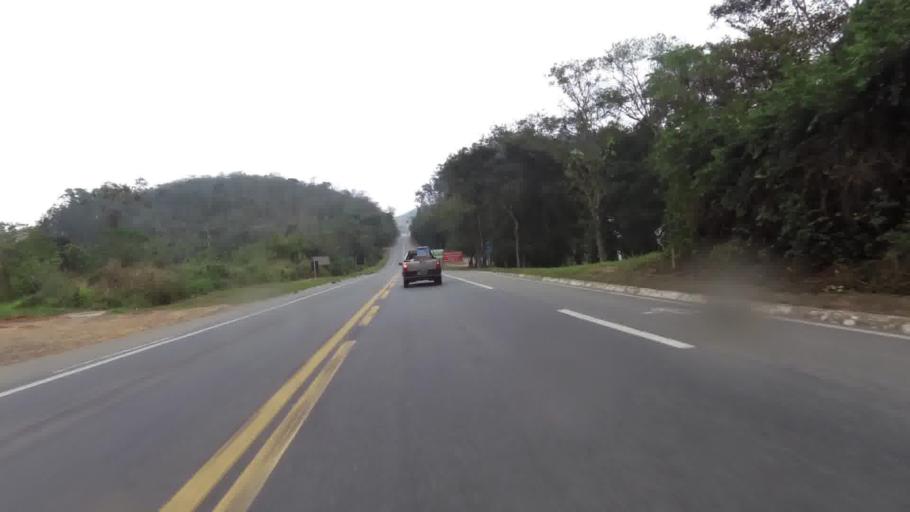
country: BR
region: Espirito Santo
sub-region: Rio Novo Do Sul
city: Rio Novo do Sul
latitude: -20.8908
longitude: -40.9984
